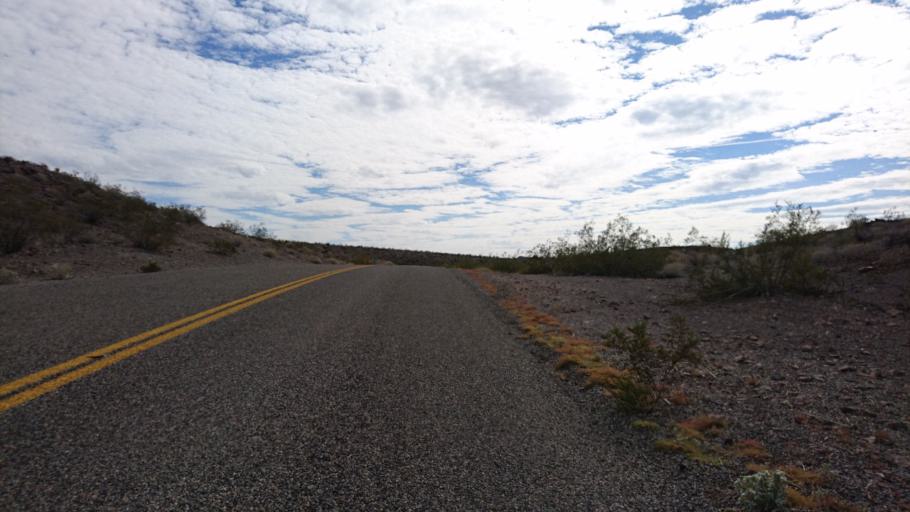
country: US
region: Arizona
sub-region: Mohave County
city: Mohave Valley
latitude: 34.9627
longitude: -114.4091
